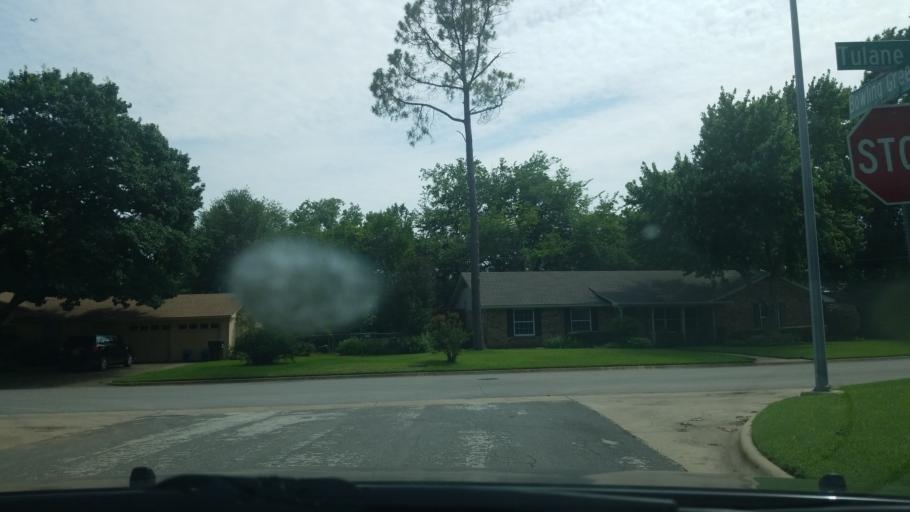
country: US
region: Texas
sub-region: Denton County
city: Denton
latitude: 33.2335
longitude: -97.1495
